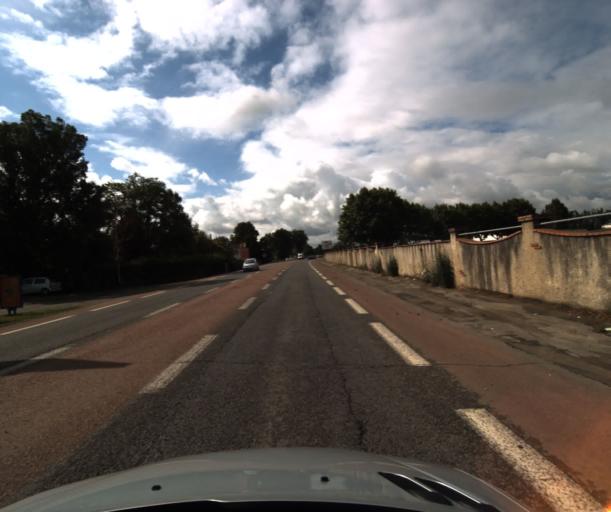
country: FR
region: Midi-Pyrenees
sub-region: Departement du Tarn-et-Garonne
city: Castelsarrasin
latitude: 44.0605
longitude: 1.0982
